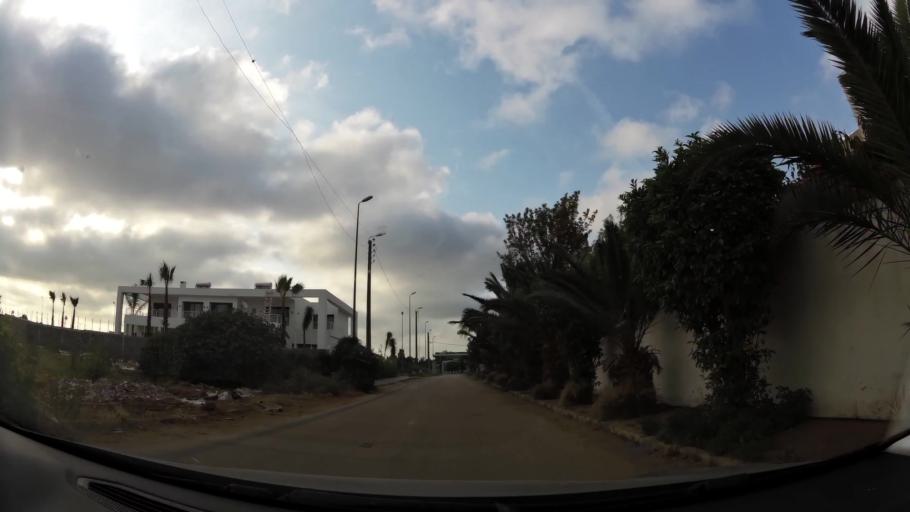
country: MA
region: Rabat-Sale-Zemmour-Zaer
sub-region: Rabat
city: Rabat
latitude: 33.9527
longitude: -6.8461
